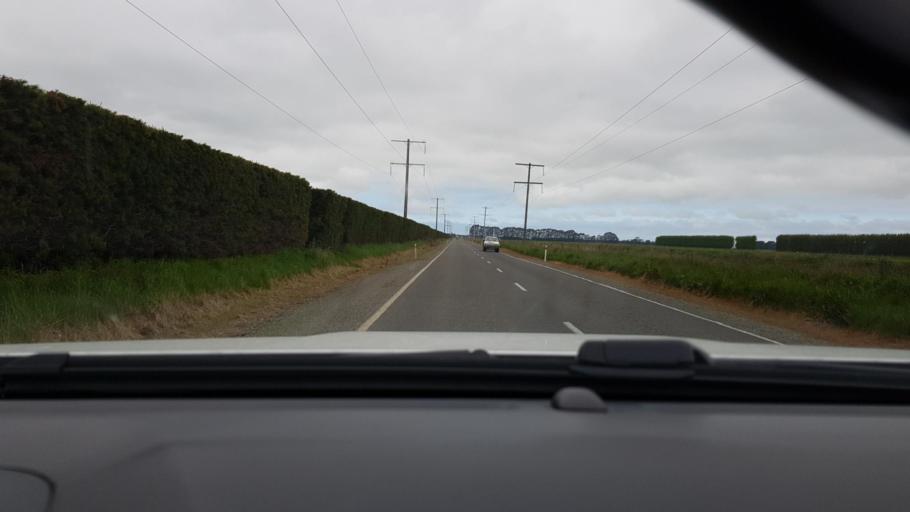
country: NZ
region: Otago
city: Oamaru
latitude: -44.9643
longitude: 171.0371
